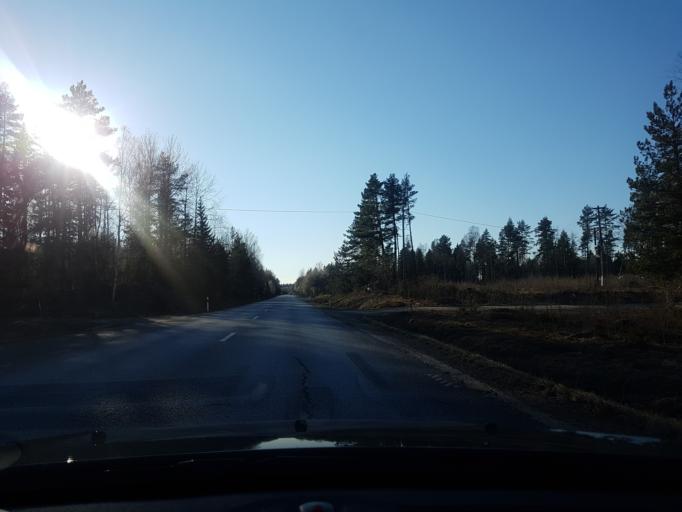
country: SE
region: Uppsala
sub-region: Enkopings Kommun
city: Orsundsbro
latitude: 59.8914
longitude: 17.1643
